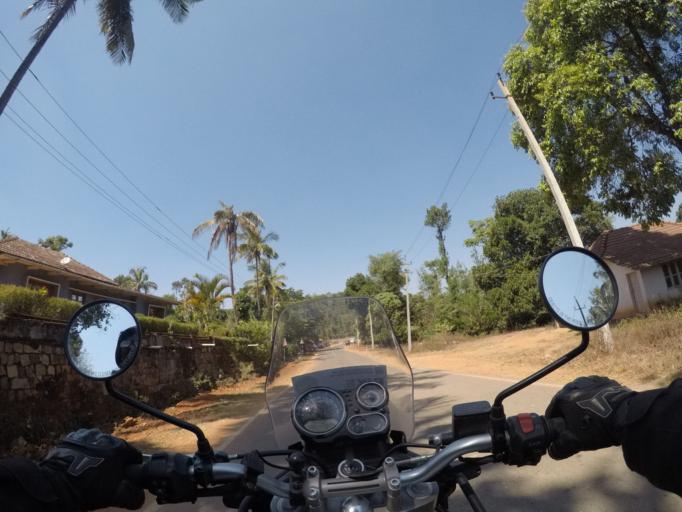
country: IN
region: Karnataka
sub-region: Chikmagalur
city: Mudigere
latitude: 13.0317
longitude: 75.6957
